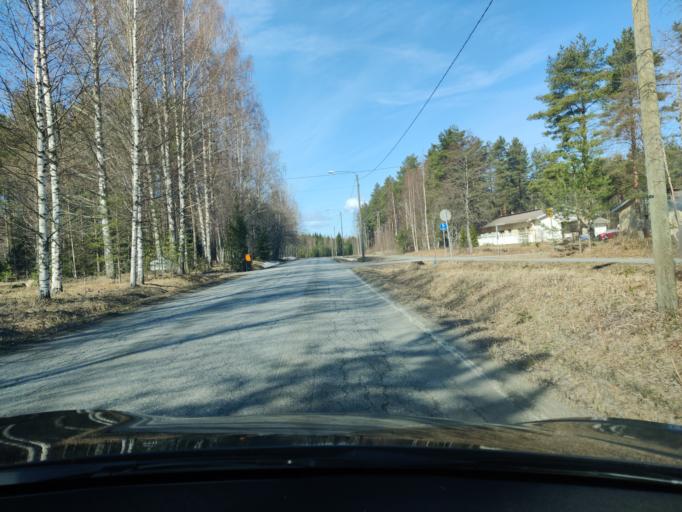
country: FI
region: Northern Savo
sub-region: Kuopio
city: Vehmersalmi
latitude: 62.7682
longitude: 27.9930
